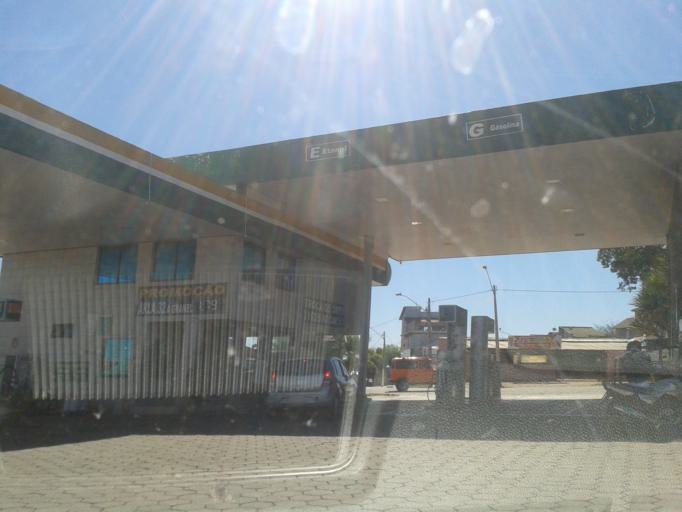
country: BR
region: Goias
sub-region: Goiania
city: Goiania
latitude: -16.6439
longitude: -49.2944
